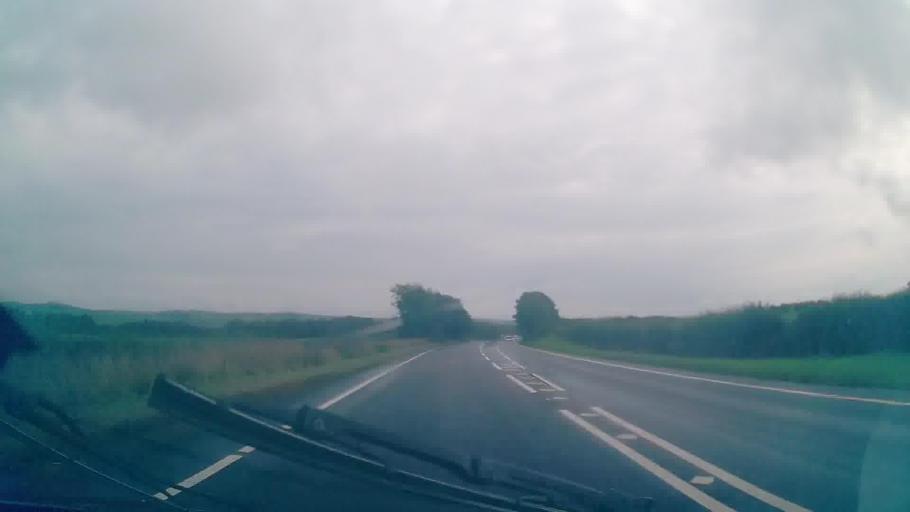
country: GB
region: Scotland
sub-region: Dumfries and Galloway
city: Locharbriggs
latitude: 55.0686
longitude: -3.5374
